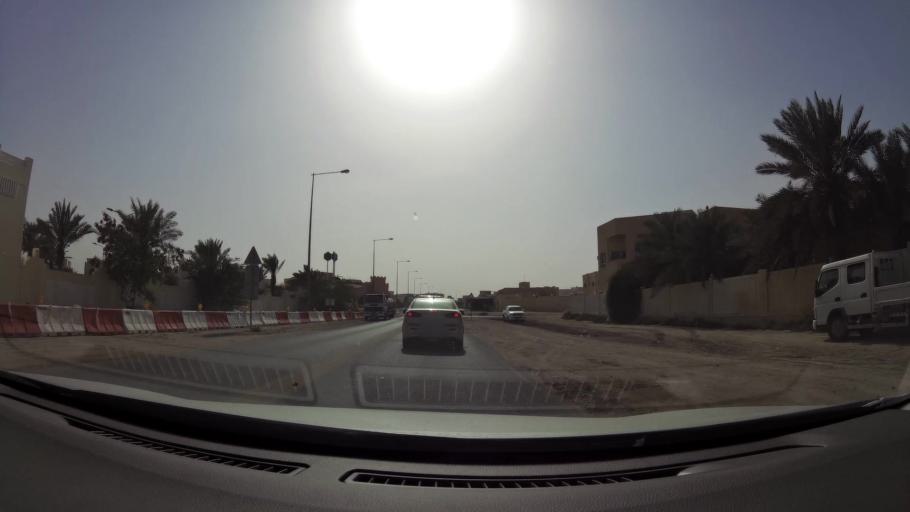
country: QA
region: Baladiyat ar Rayyan
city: Ar Rayyan
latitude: 25.3403
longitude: 51.4298
